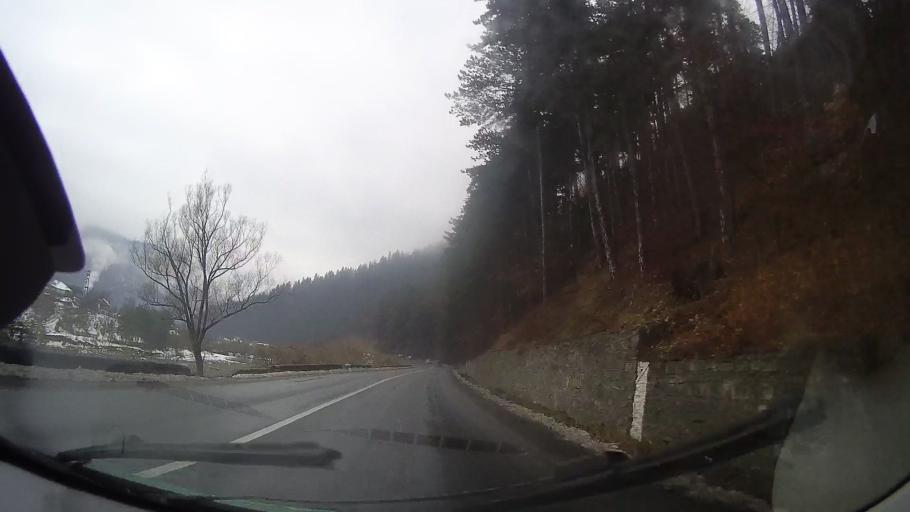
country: RO
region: Neamt
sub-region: Comuna Tarcau
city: Tarcau
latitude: 46.8923
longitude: 26.1397
